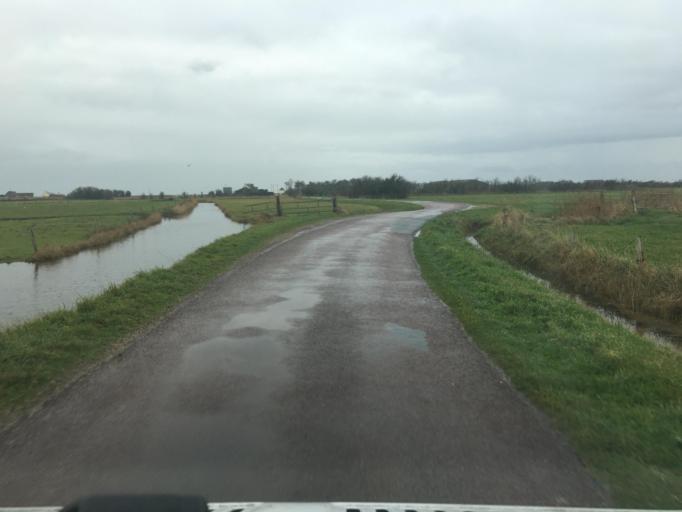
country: FR
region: Lower Normandy
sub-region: Departement de la Manche
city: Sainte-Mere-Eglise
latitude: 49.4507
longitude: -1.2272
